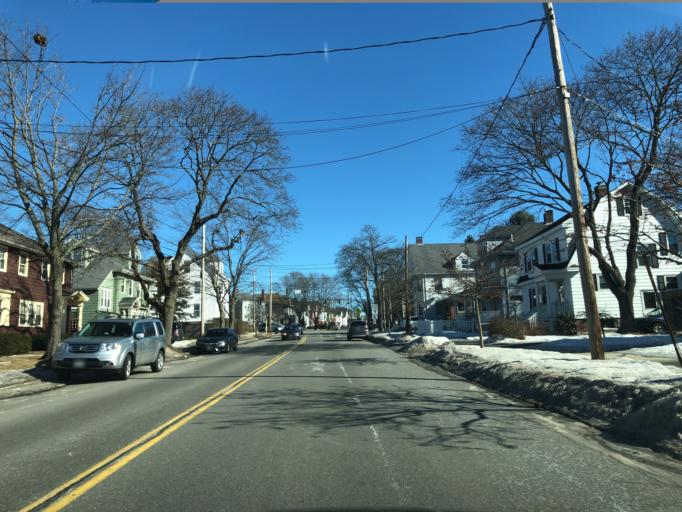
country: US
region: Maine
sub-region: Cumberland County
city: South Portland Gardens
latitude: 43.6697
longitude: -70.2964
